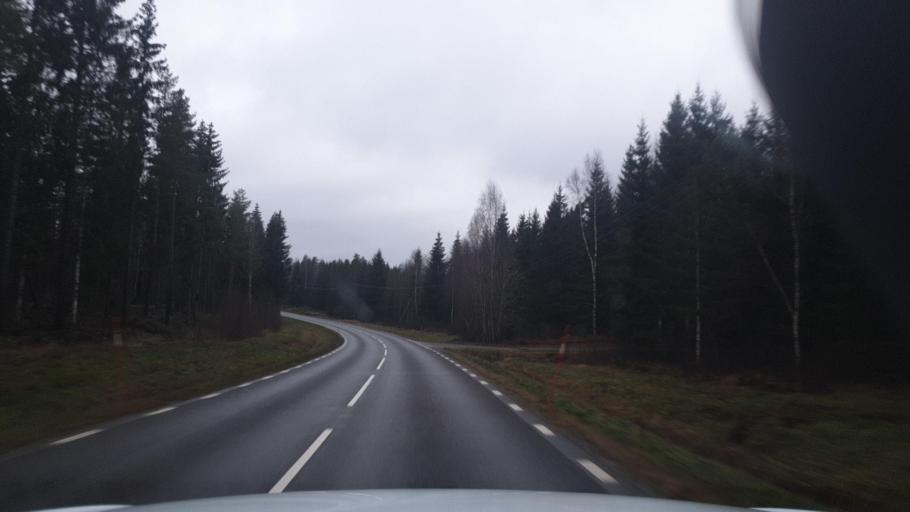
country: SE
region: Vaermland
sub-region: Arvika Kommun
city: Arvika
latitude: 59.7287
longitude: 12.5654
